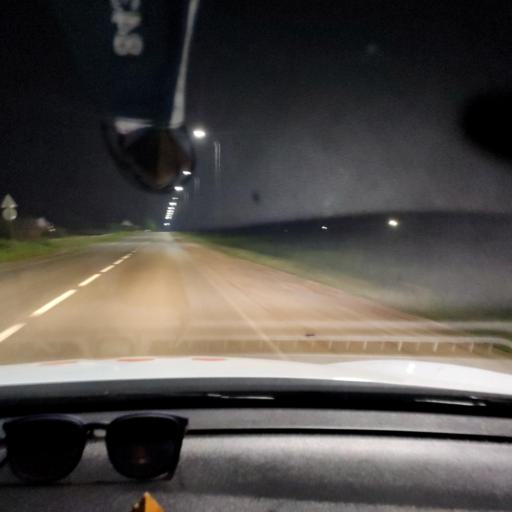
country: RU
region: Tatarstan
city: Rybnaya Sloboda
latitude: 55.4684
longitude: 50.1640
